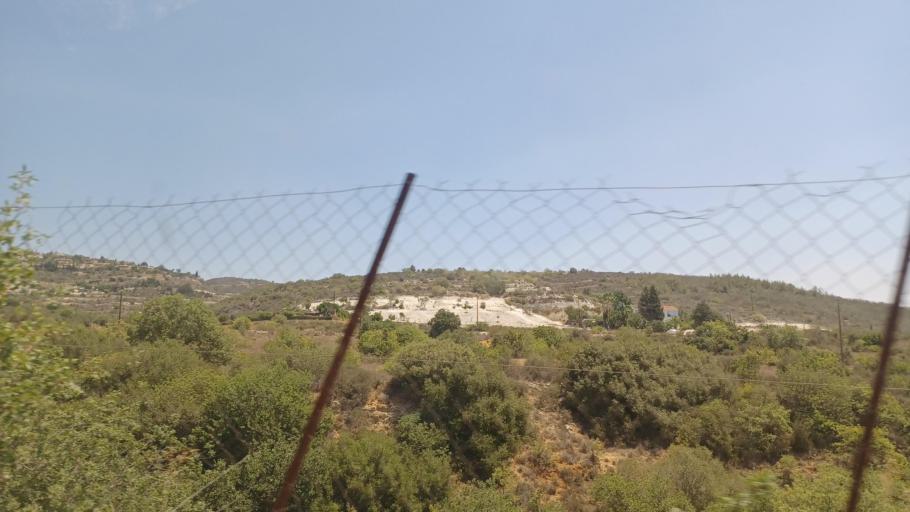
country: CY
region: Pafos
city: Mesogi
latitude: 34.8236
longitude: 32.4593
